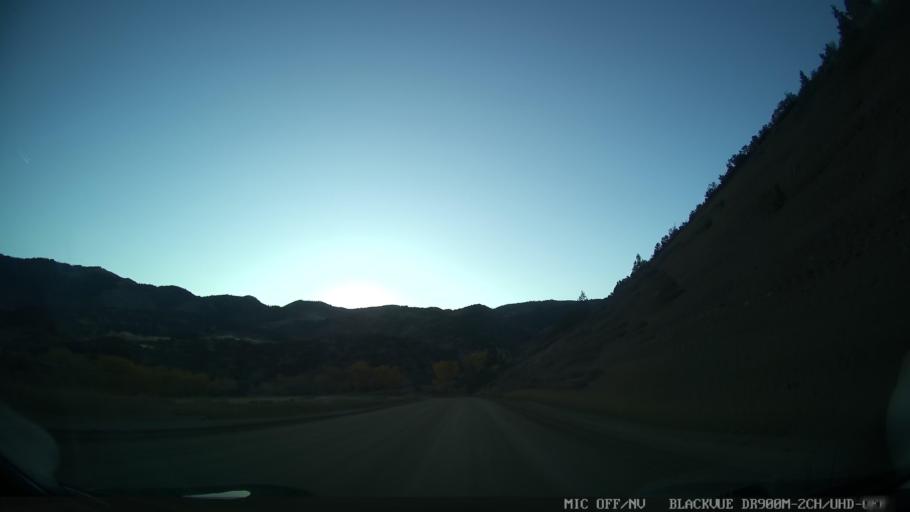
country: US
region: Colorado
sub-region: Grand County
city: Kremmling
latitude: 39.9657
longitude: -106.5077
